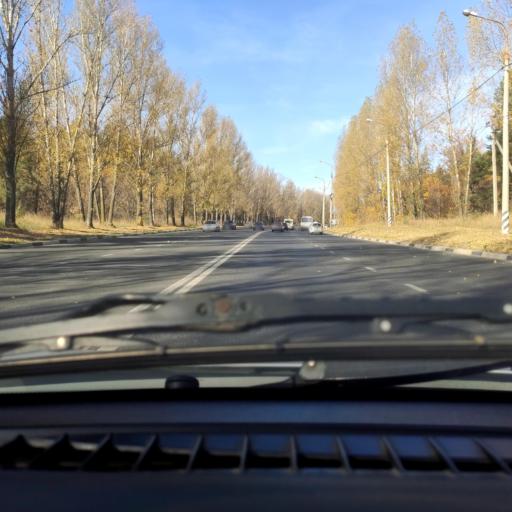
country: RU
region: Samara
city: Zhigulevsk
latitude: 53.5039
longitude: 49.4692
